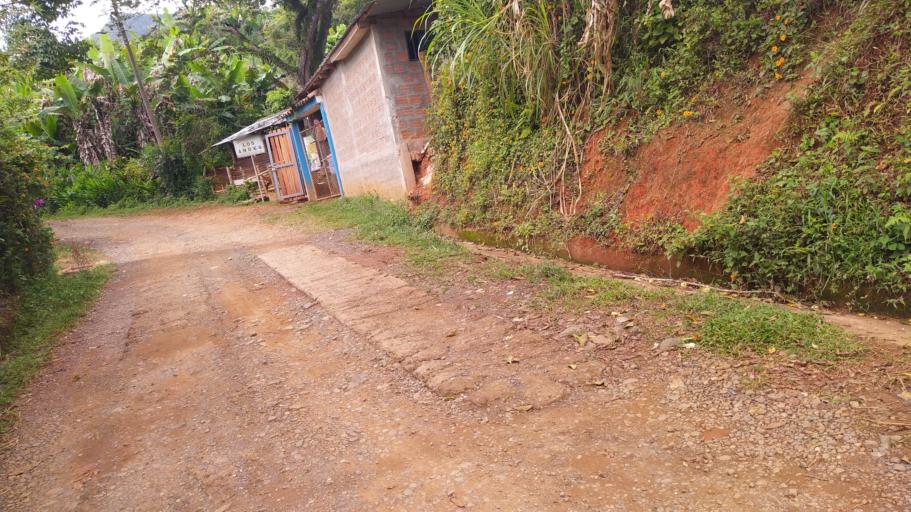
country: CO
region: Valle del Cauca
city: Cali
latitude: 3.4281
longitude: -76.6167
